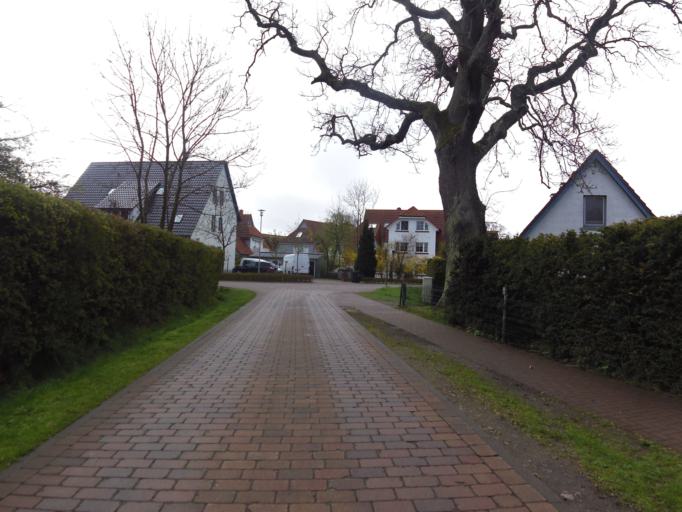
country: DE
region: Mecklenburg-Vorpommern
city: Zingst
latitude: 54.4376
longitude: 12.6800
